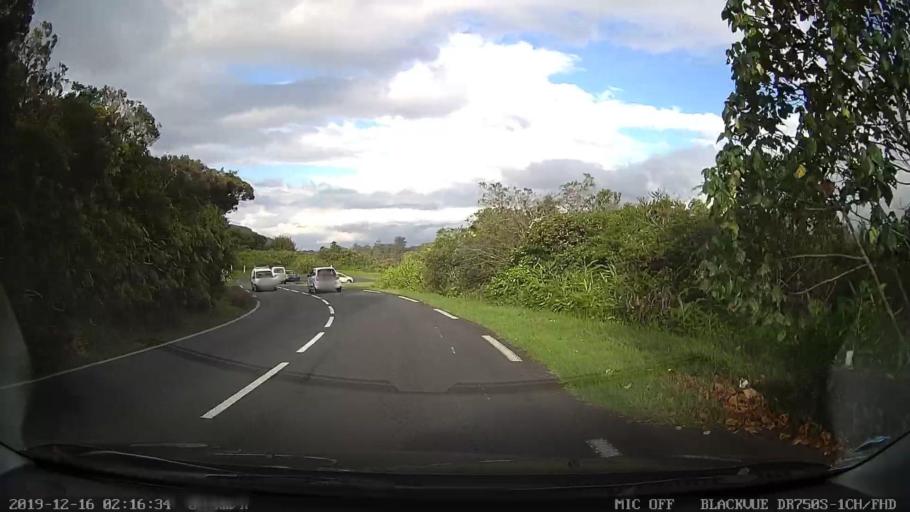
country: RE
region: Reunion
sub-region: Reunion
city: Cilaos
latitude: -21.1554
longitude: 55.6019
